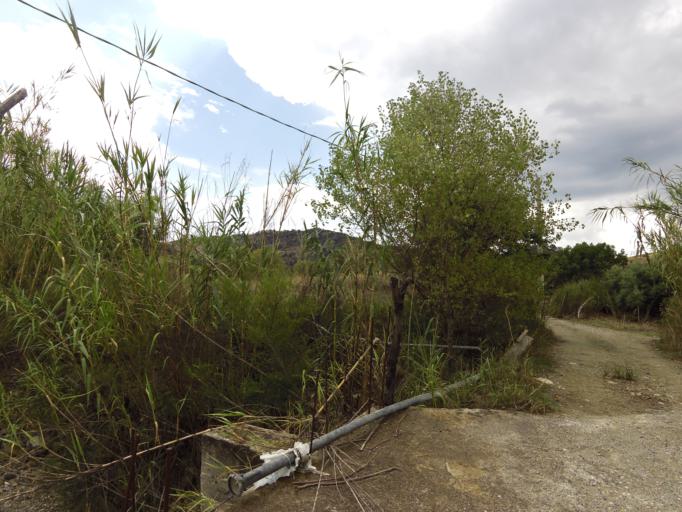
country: IT
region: Calabria
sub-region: Provincia di Reggio Calabria
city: Stilo
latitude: 38.4545
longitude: 16.4672
